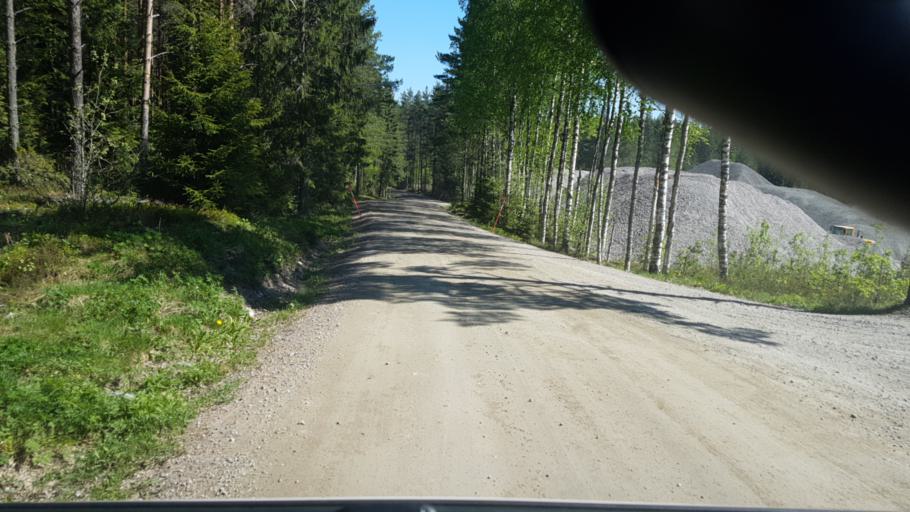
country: SE
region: Vaermland
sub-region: Arvika Kommun
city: Arvika
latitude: 59.8320
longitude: 12.6061
